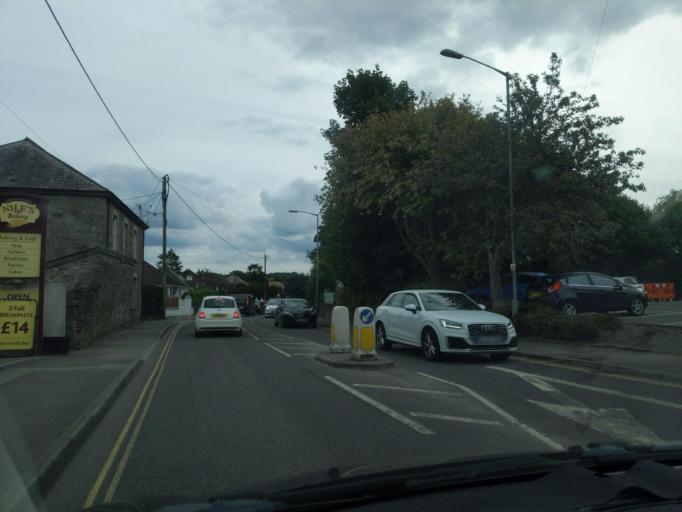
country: GB
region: England
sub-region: Cornwall
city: St Austell
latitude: 50.3332
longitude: -4.7931
